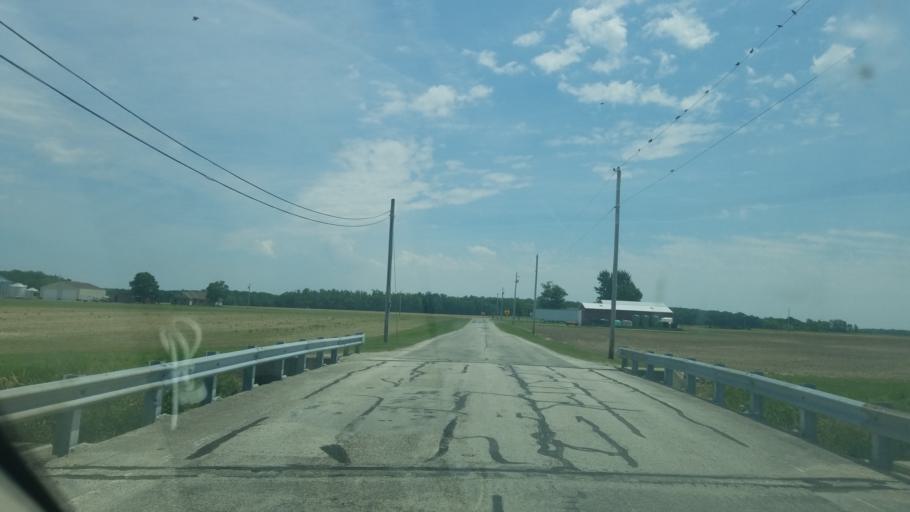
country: US
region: Ohio
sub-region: Wood County
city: North Baltimore
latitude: 41.2218
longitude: -83.5958
